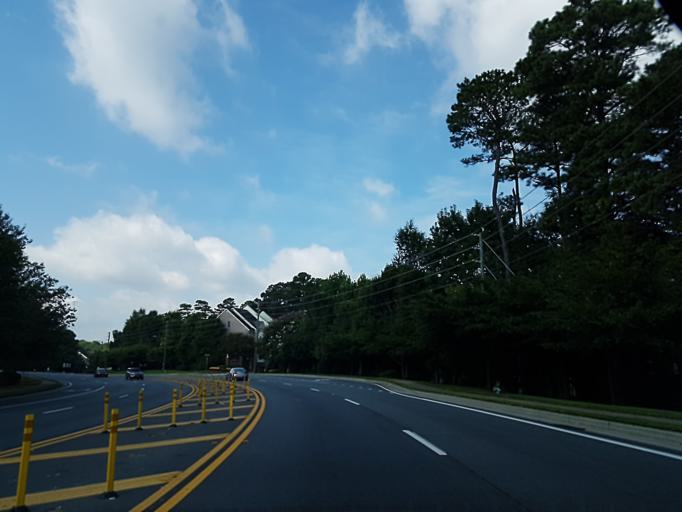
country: US
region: Georgia
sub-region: DeKalb County
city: North Druid Hills
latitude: 33.8175
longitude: -84.3155
